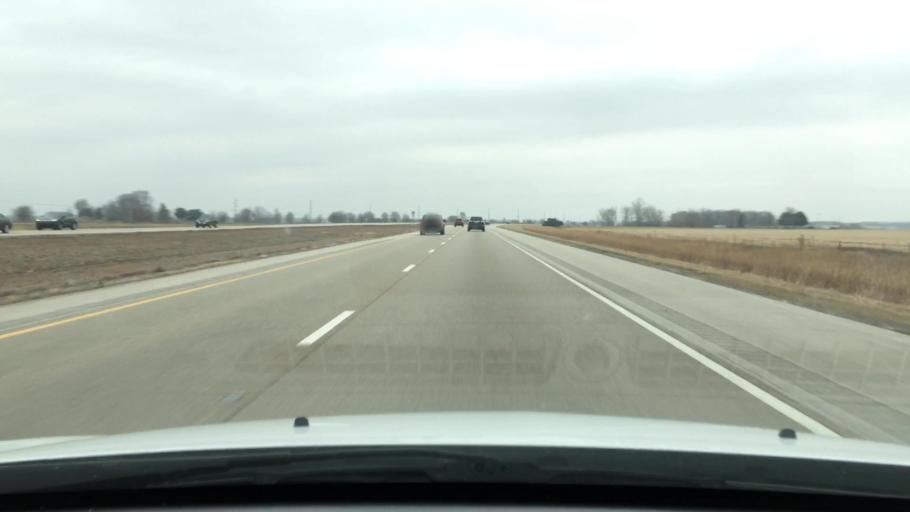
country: US
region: Illinois
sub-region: Logan County
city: Lincoln
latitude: 40.1934
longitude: -89.3058
